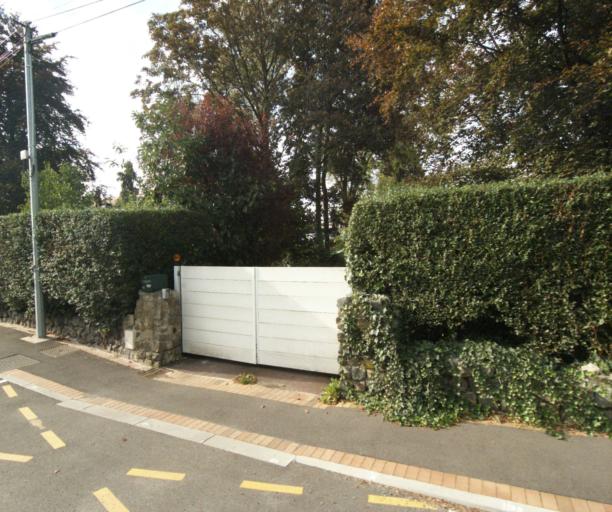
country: FR
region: Nord-Pas-de-Calais
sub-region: Departement du Nord
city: Hallennes-lez-Haubourdin
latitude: 50.6169
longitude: 2.9629
